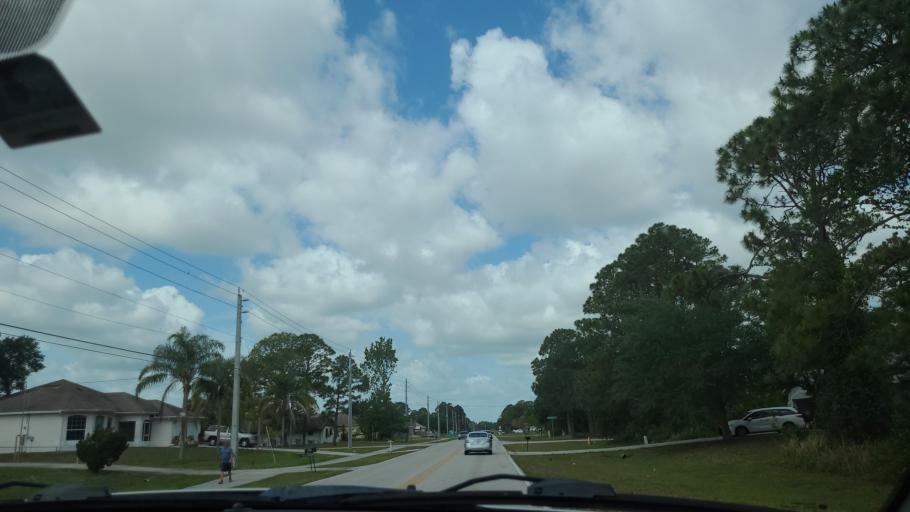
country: US
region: Florida
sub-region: Brevard County
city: June Park
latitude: 27.9875
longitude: -80.6803
